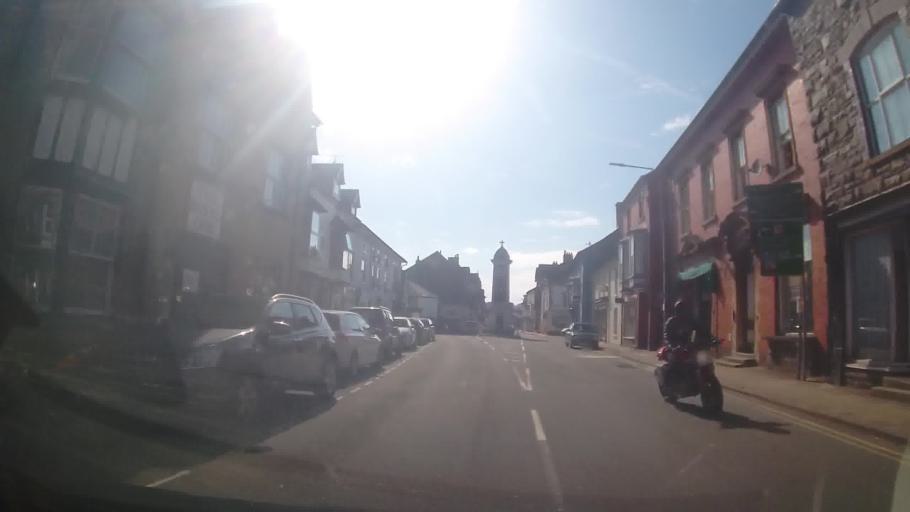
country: GB
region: Wales
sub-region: Sir Powys
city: Rhayader
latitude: 52.3008
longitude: -3.5096
